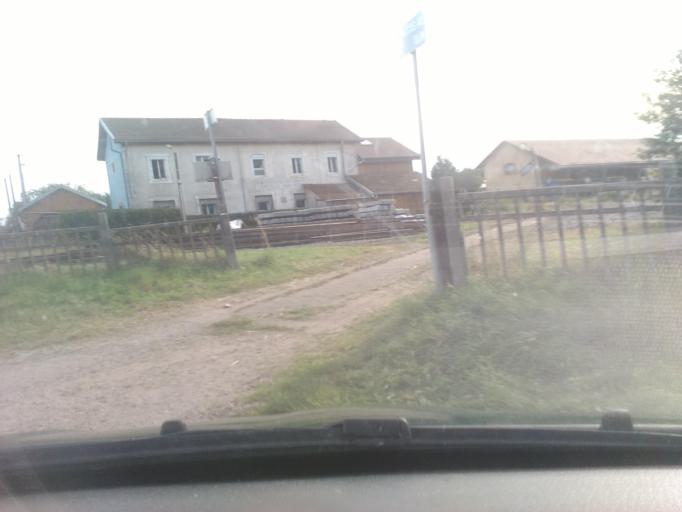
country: FR
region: Lorraine
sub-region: Departement des Vosges
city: Corcieux
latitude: 48.1987
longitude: 6.8778
